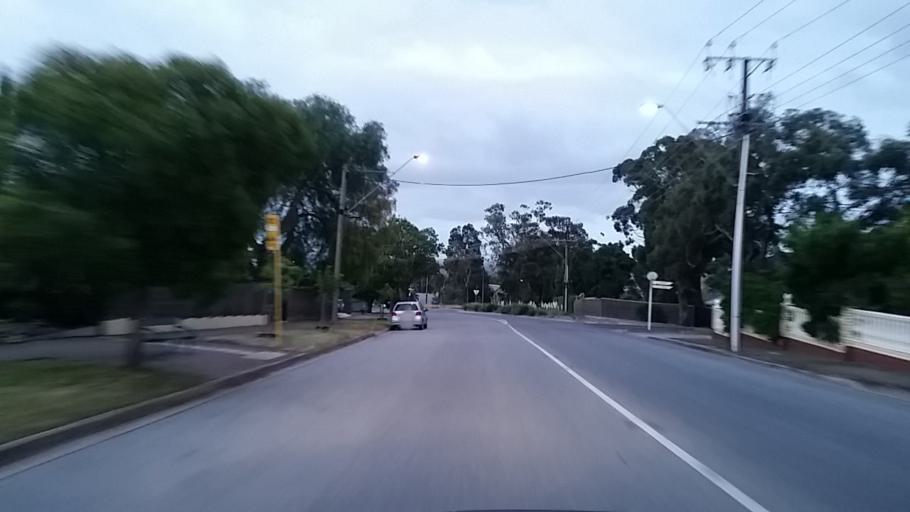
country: AU
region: South Australia
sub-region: Burnside
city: Hazelwood Park
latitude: -34.9384
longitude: 138.6704
